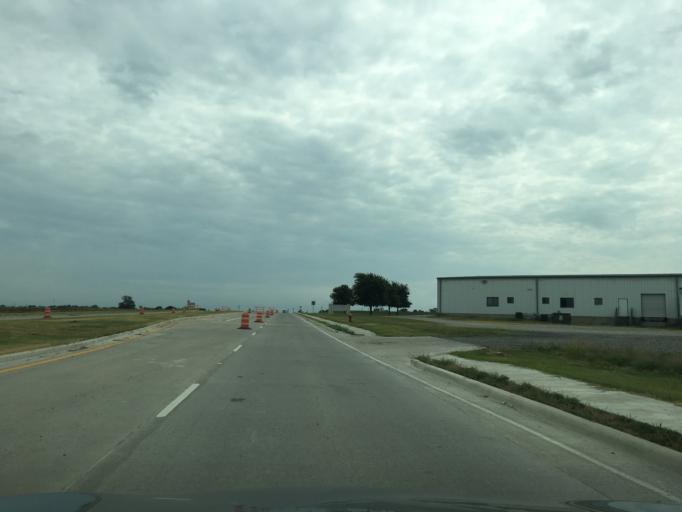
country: US
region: Texas
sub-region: Collin County
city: Melissa
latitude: 33.3004
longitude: -96.5325
